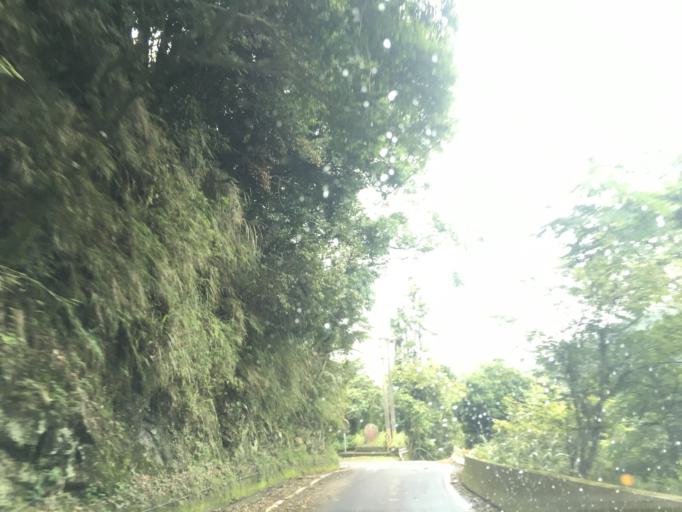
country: TW
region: Taiwan
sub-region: Yunlin
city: Douliu
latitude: 23.5644
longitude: 120.6179
